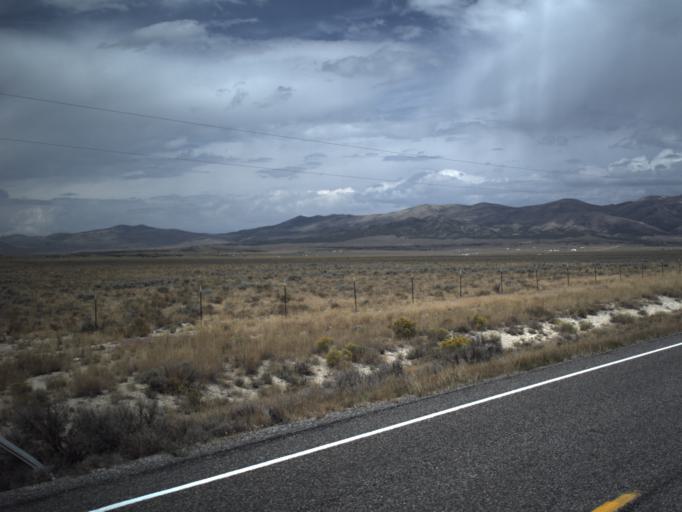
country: US
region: Idaho
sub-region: Cassia County
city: Burley
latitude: 41.7483
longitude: -113.5167
